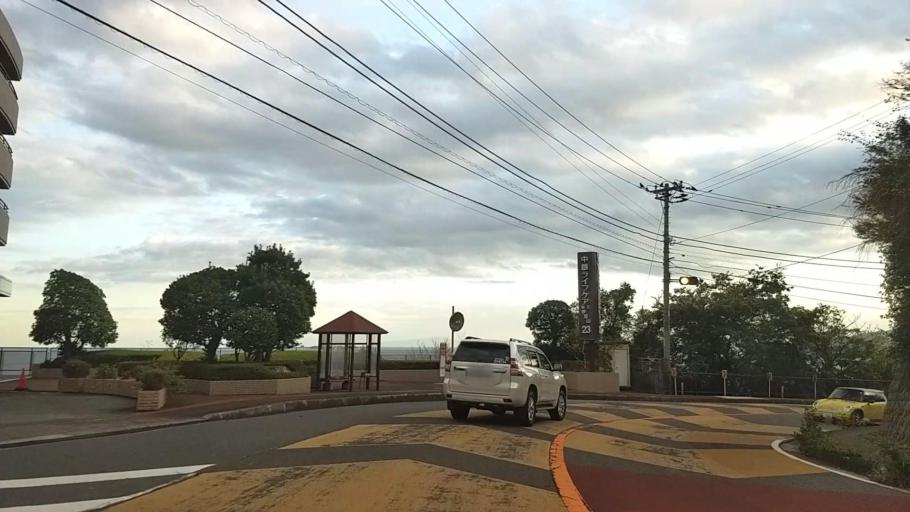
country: JP
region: Shizuoka
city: Atami
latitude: 35.1152
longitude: 139.0890
